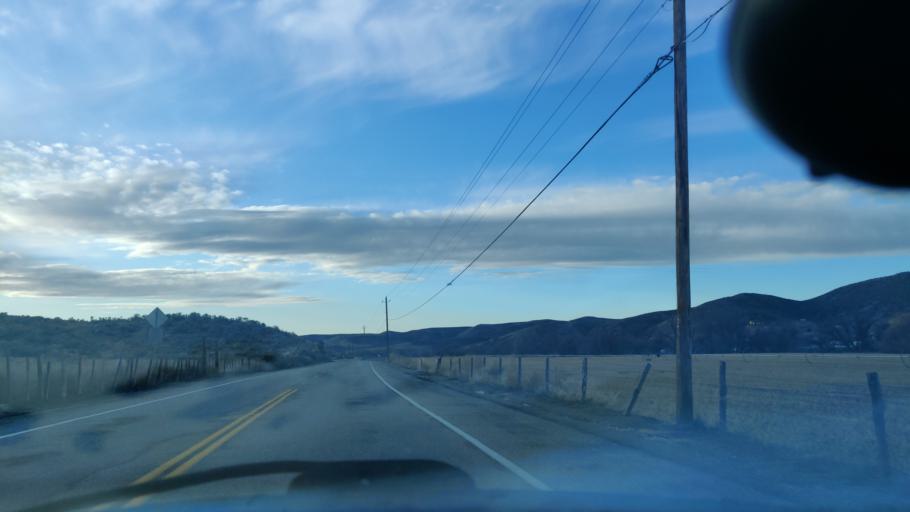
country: US
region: Idaho
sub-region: Ada County
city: Eagle
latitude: 43.7294
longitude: -116.2905
